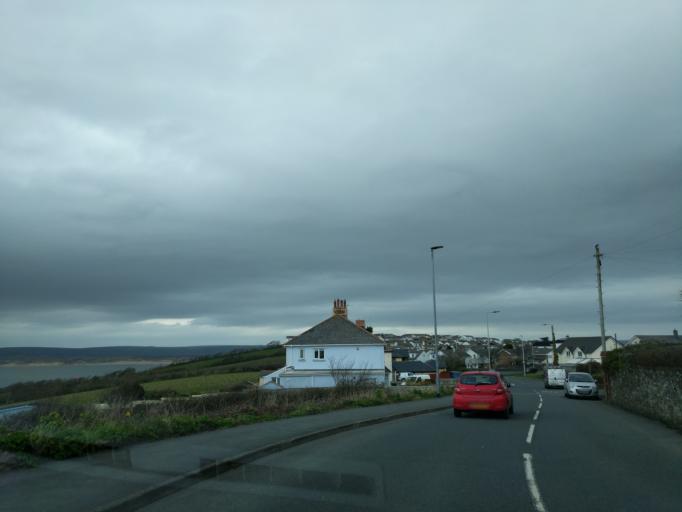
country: GB
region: England
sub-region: Devon
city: Appledore
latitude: 51.0504
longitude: -4.2009
